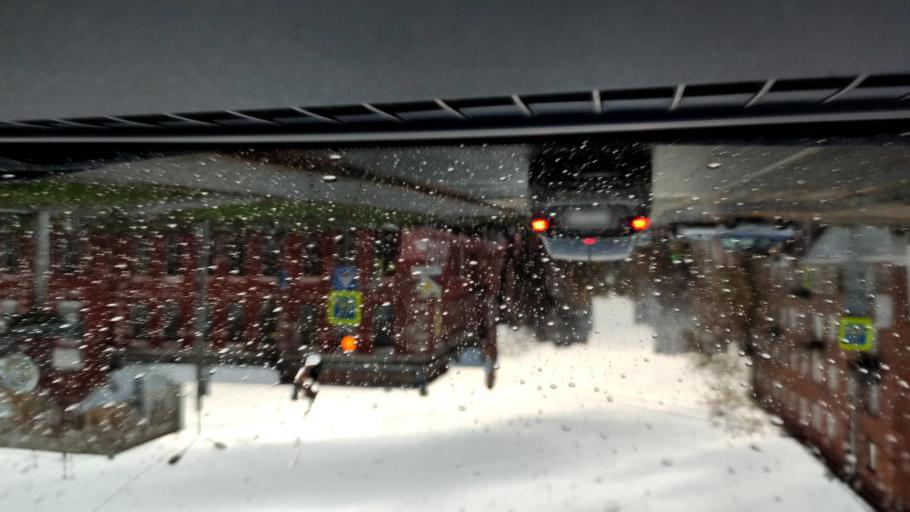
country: RU
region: Perm
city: Perm
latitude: 58.0041
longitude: 56.2070
